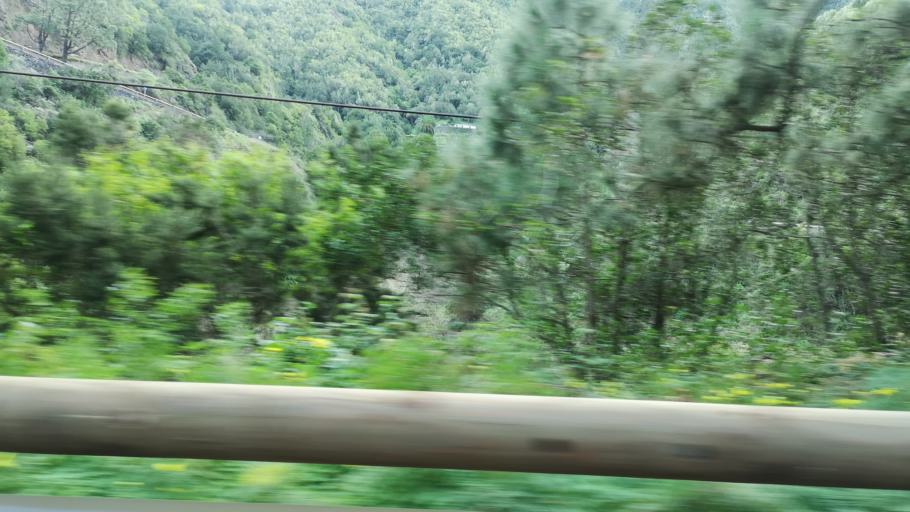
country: ES
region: Canary Islands
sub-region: Provincia de Santa Cruz de Tenerife
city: Hermigua
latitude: 28.1347
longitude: -17.2016
